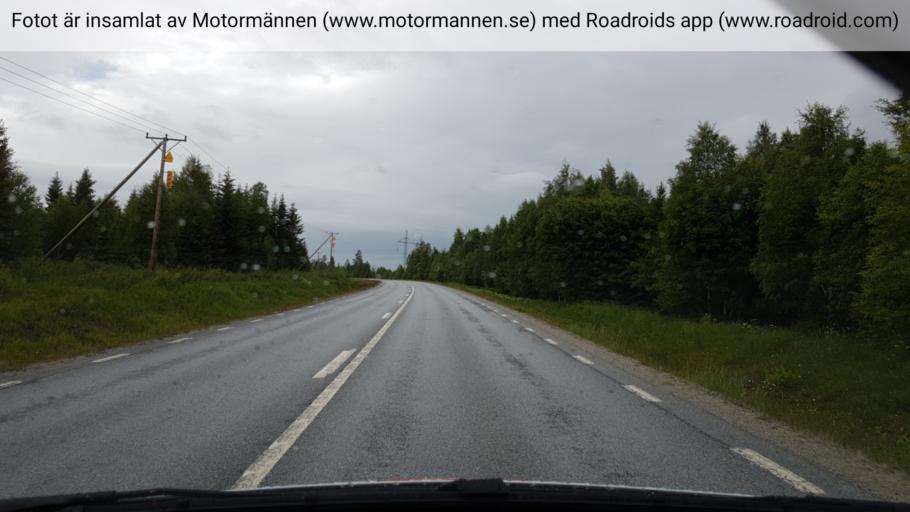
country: SE
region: Vaesterbotten
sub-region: Bjurholms Kommun
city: Bjurholm
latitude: 63.9349
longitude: 19.3300
